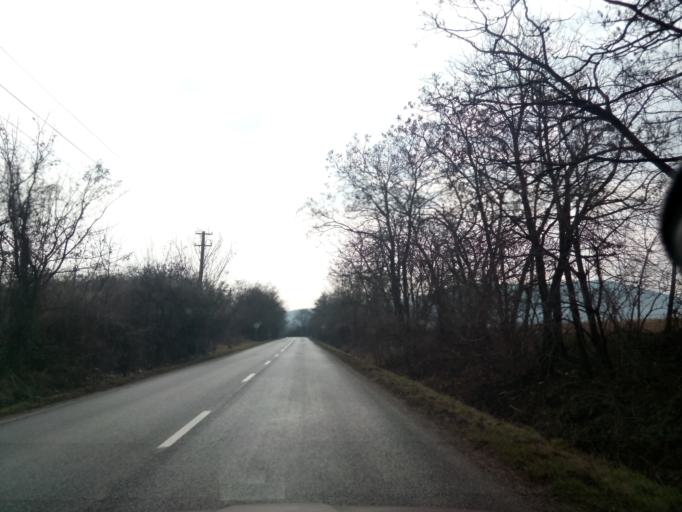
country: SK
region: Kosicky
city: Kosice
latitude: 48.6497
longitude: 21.4093
